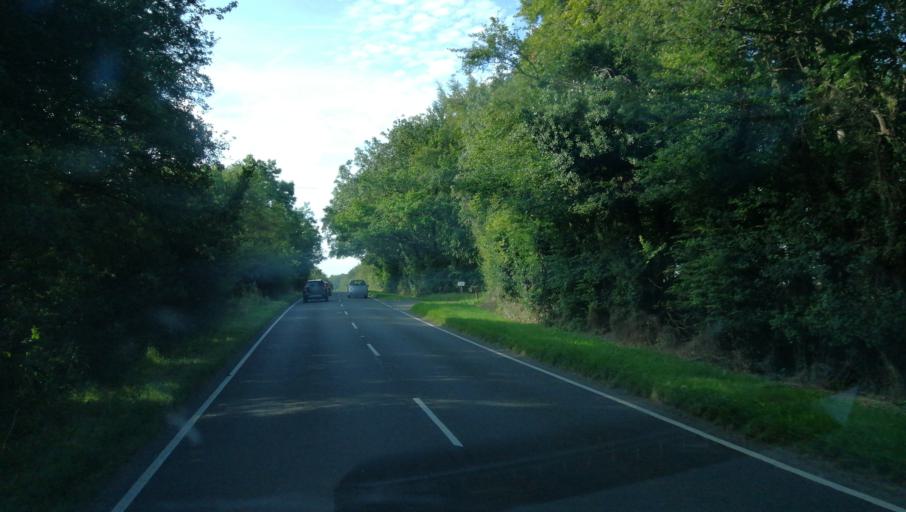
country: GB
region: England
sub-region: Oxfordshire
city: Woodstock
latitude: 51.9053
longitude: -1.3288
